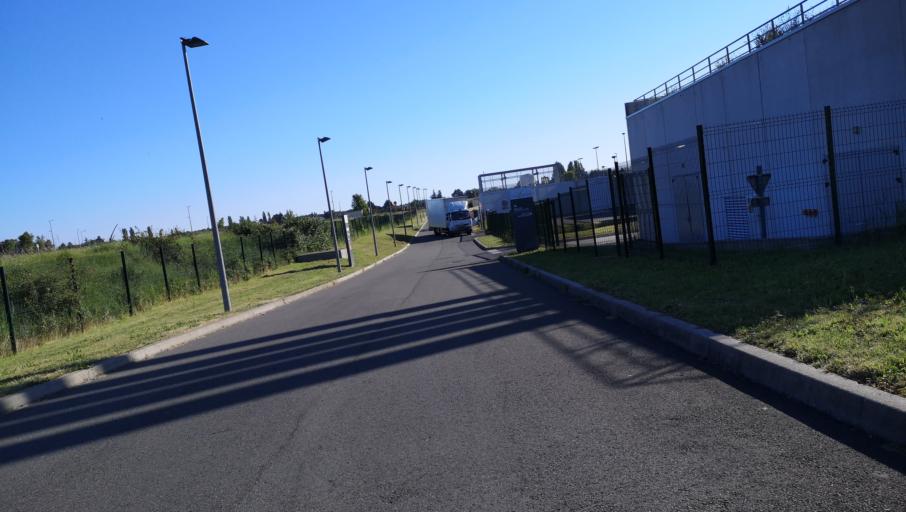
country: FR
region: Centre
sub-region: Departement du Loiret
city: Saran
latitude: 47.9400
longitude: 1.8769
